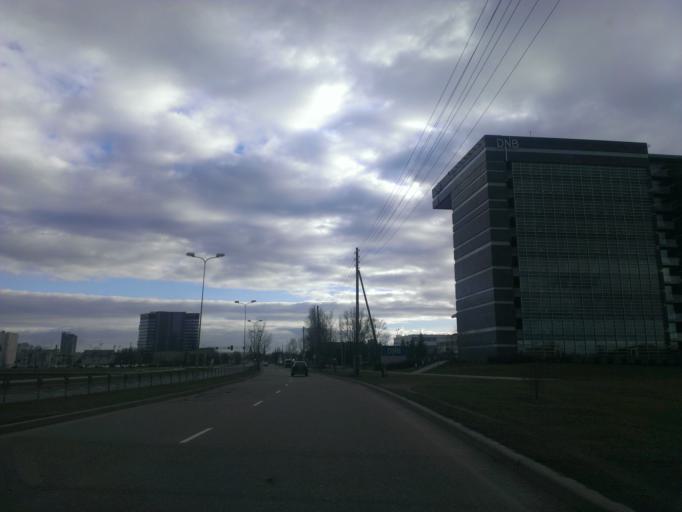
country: LV
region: Riga
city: Riga
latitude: 56.9715
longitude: 24.1206
